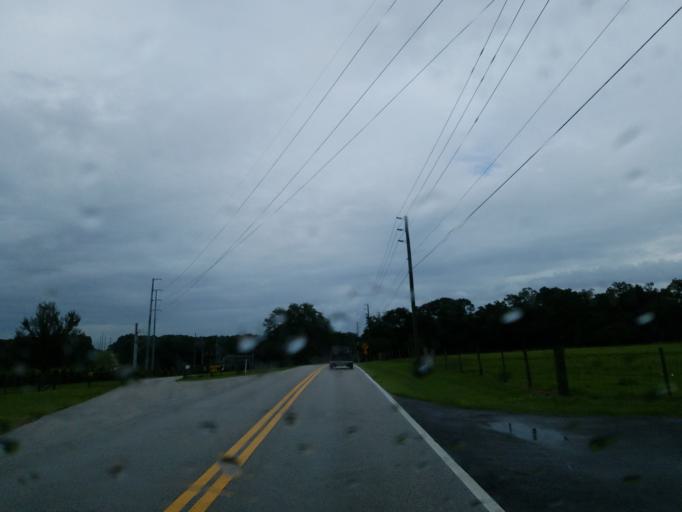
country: US
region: Florida
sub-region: Hernando County
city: Brooksville
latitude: 28.5837
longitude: -82.3443
